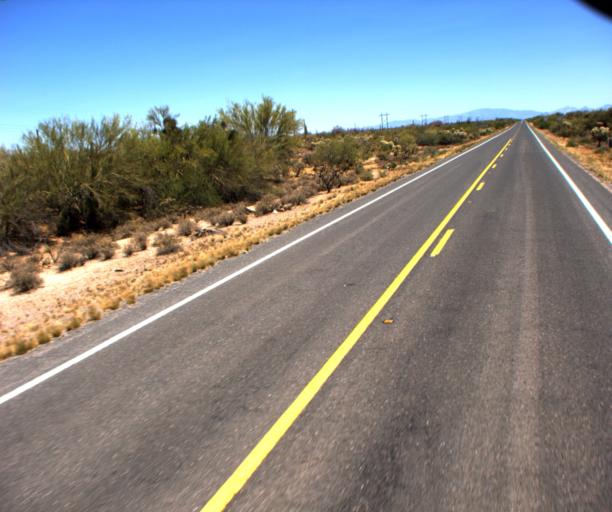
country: US
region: Arizona
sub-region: Pinal County
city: Florence
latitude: 32.8472
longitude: -111.2277
